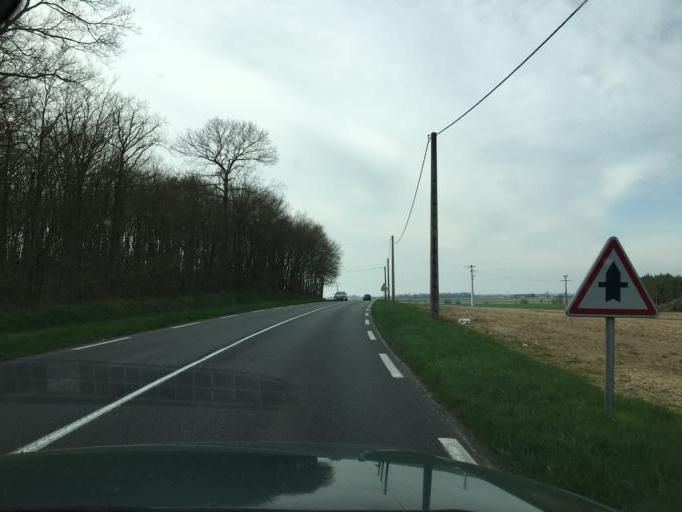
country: FR
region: Centre
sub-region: Departement du Loiret
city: Vienne-en-Val
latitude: 47.8030
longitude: 2.1219
